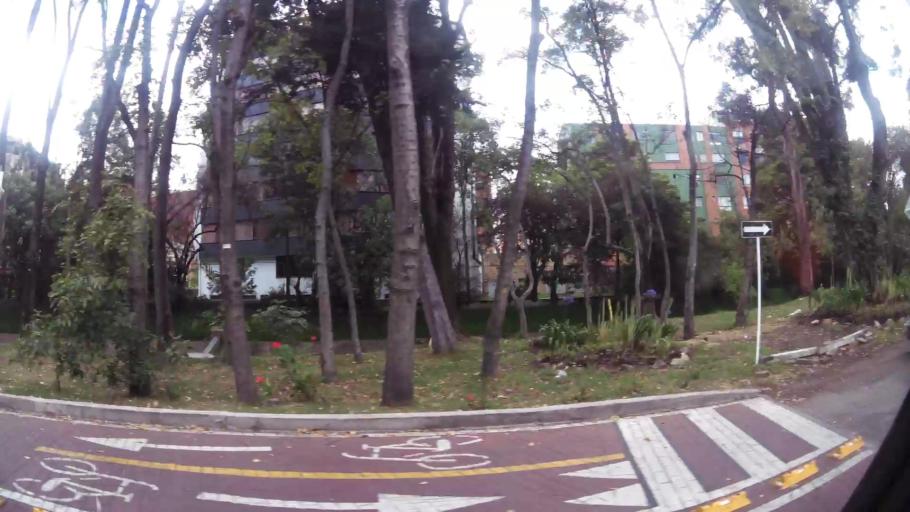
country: CO
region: Bogota D.C.
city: Bogota
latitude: 4.6360
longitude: -74.0764
